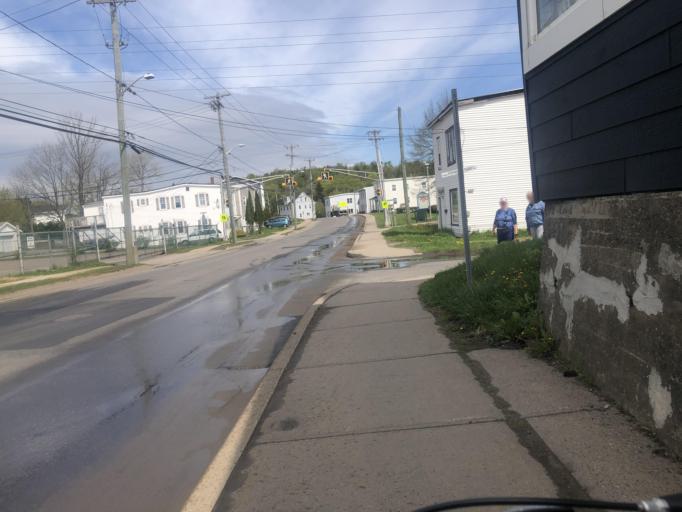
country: CA
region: New Brunswick
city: Saint John
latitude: 45.2824
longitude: -66.0821
